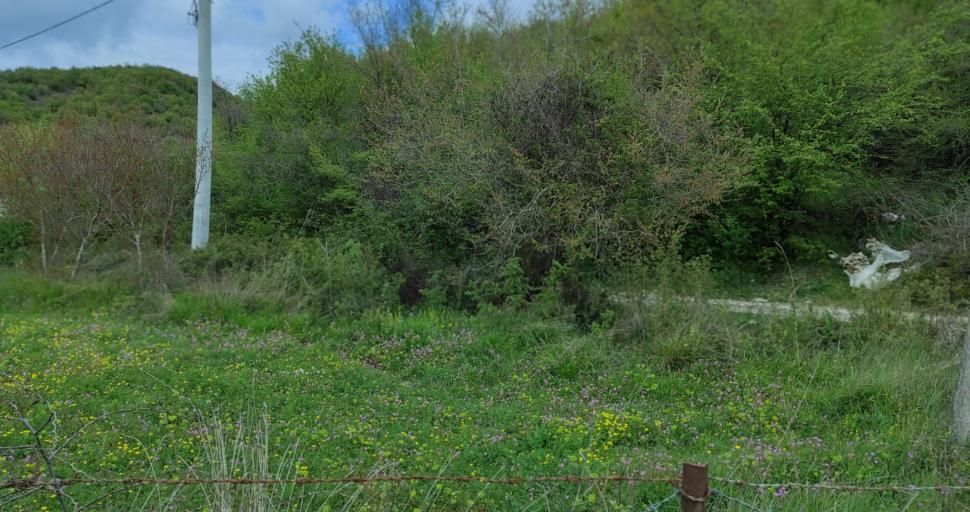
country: AL
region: Shkoder
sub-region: Rrethi i Shkodres
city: Dajc
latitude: 42.0263
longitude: 19.4206
